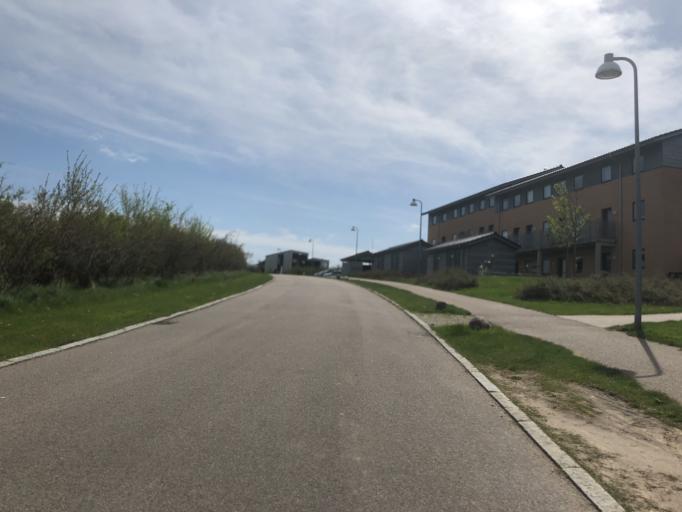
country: DK
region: Zealand
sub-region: Ringsted Kommune
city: Ringsted
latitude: 55.4509
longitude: 11.8215
